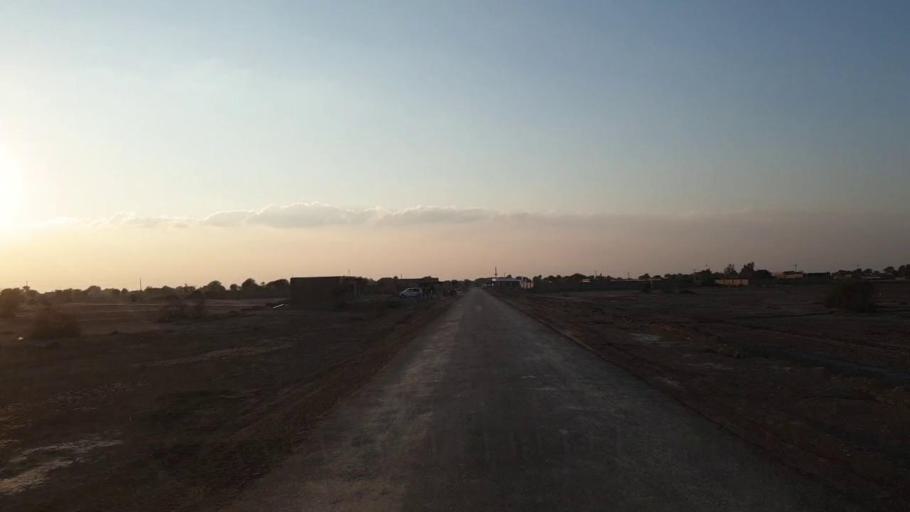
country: PK
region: Sindh
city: Shahpur Chakar
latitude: 26.1576
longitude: 68.5467
